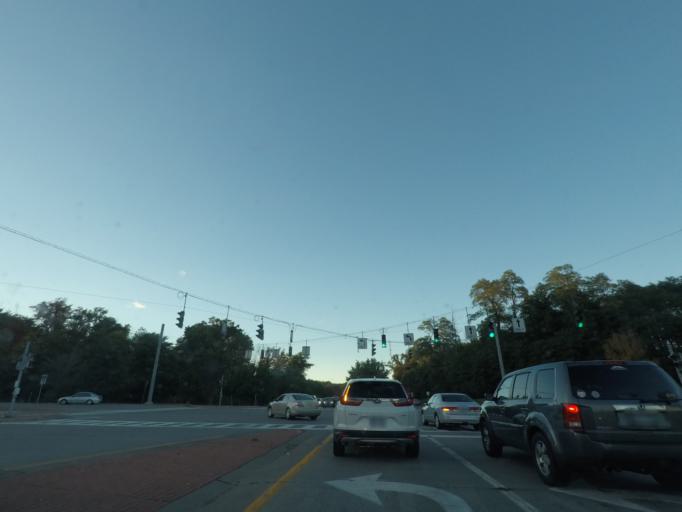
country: US
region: New York
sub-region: Albany County
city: Colonie
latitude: 42.7455
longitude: -73.8161
